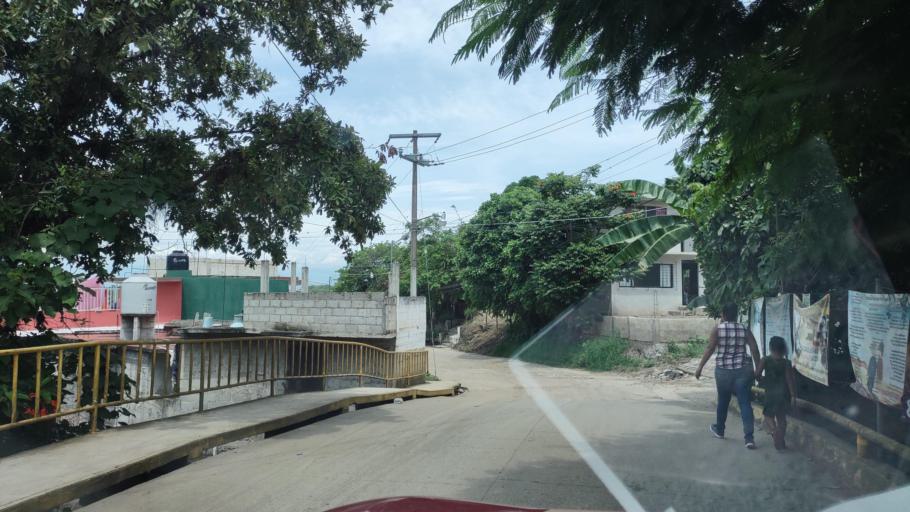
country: MX
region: Veracruz
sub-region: Emiliano Zapata
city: Jacarandas
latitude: 19.4662
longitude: -96.8348
